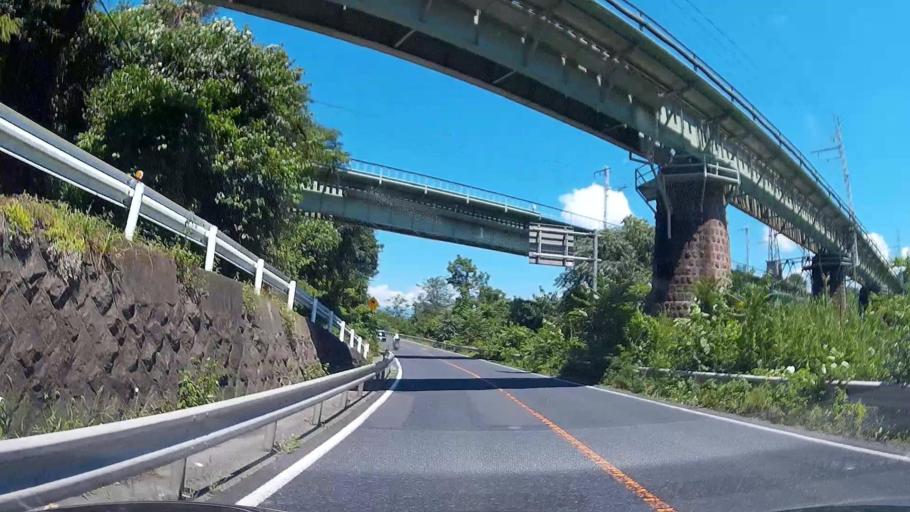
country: JP
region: Gunma
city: Numata
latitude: 36.6300
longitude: 139.0385
